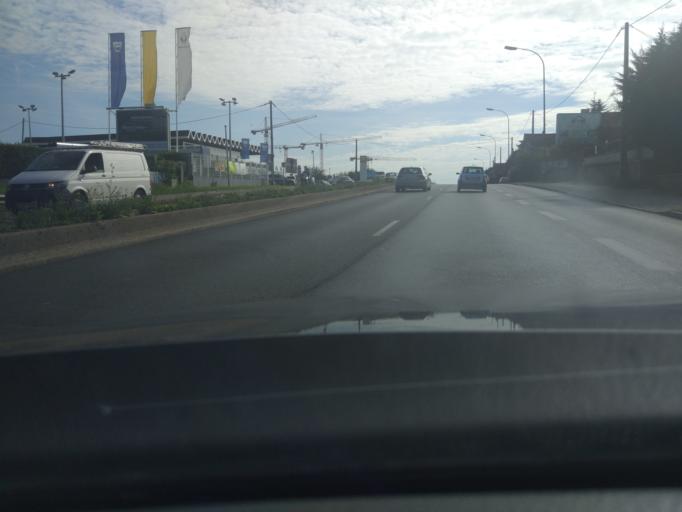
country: FR
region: Ile-de-France
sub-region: Departement de l'Essonne
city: La Ville-du-Bois
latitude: 48.6487
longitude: 2.2715
